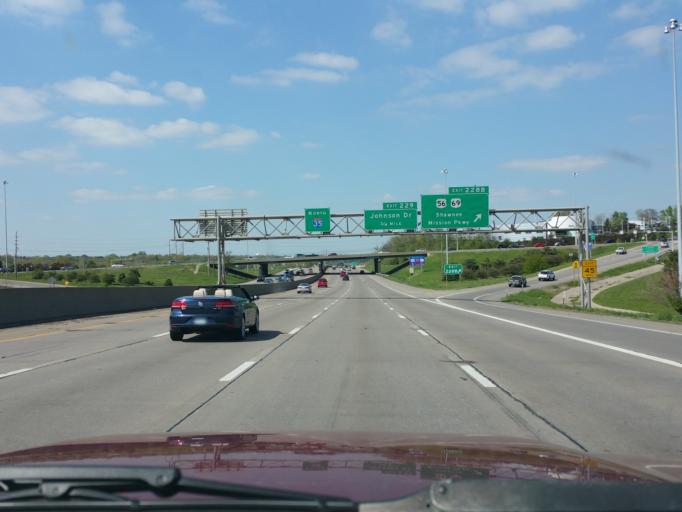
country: US
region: Kansas
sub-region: Johnson County
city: Merriam
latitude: 39.0122
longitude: -94.6933
